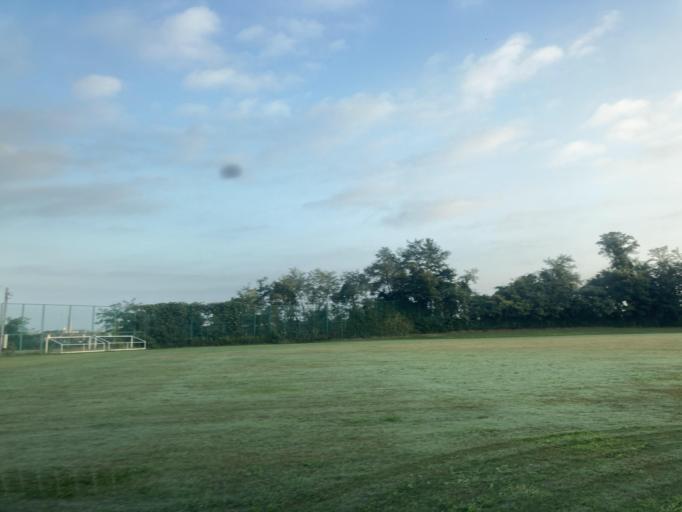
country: JP
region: Tokyo
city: Kokubunji
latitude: 35.6502
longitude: 139.4814
